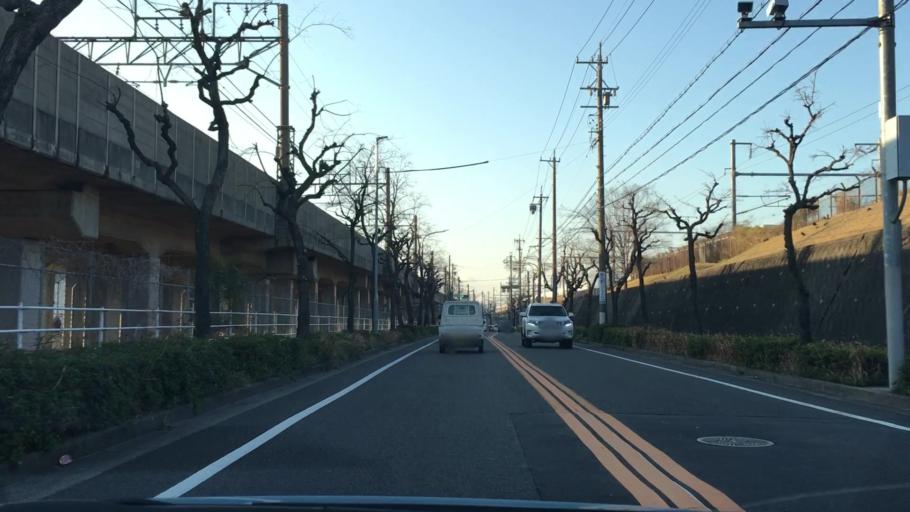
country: JP
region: Aichi
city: Obu
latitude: 35.0594
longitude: 136.9460
